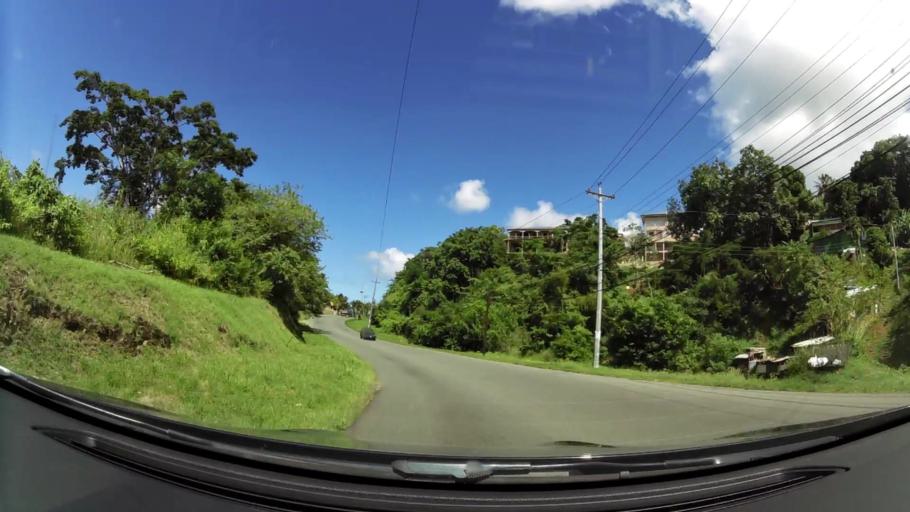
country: TT
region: Tobago
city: Scarborough
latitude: 11.1987
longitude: -60.7923
